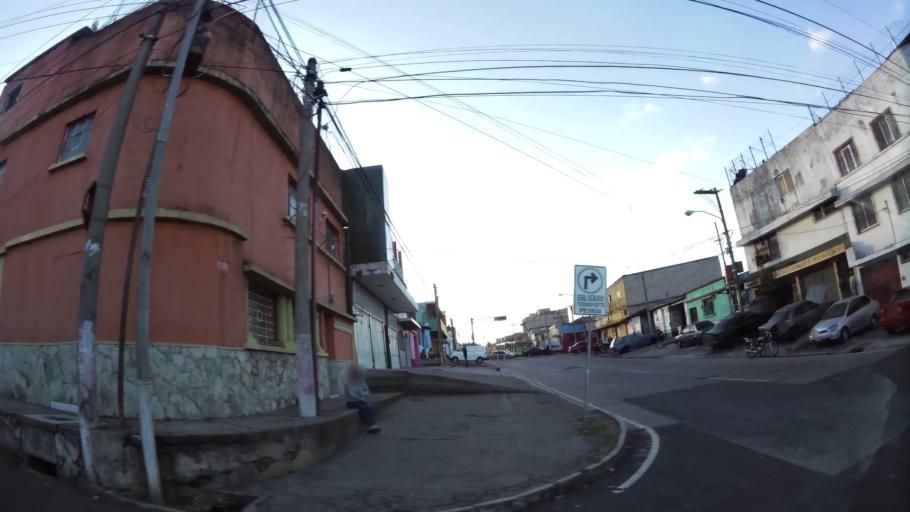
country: GT
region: Guatemala
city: Guatemala City
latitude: 14.6254
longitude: -90.5206
